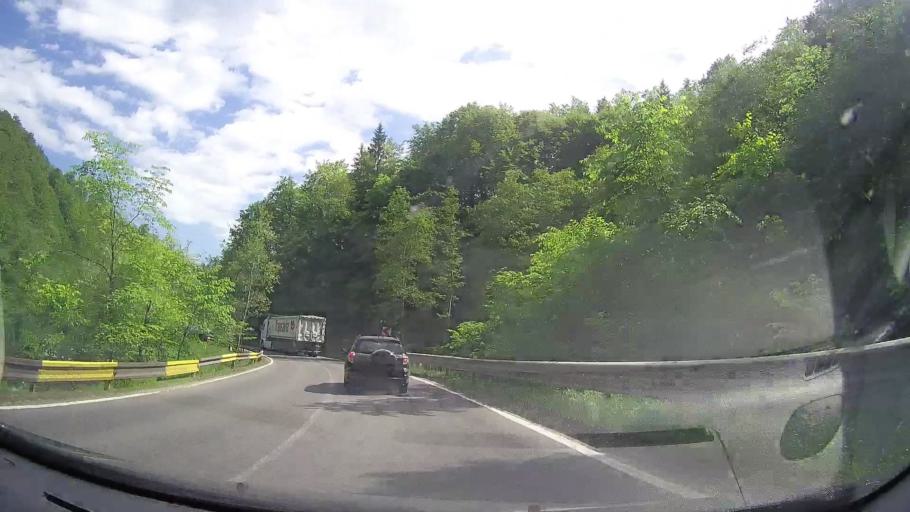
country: RO
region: Prahova
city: Maneciu
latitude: 45.3798
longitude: 25.9293
